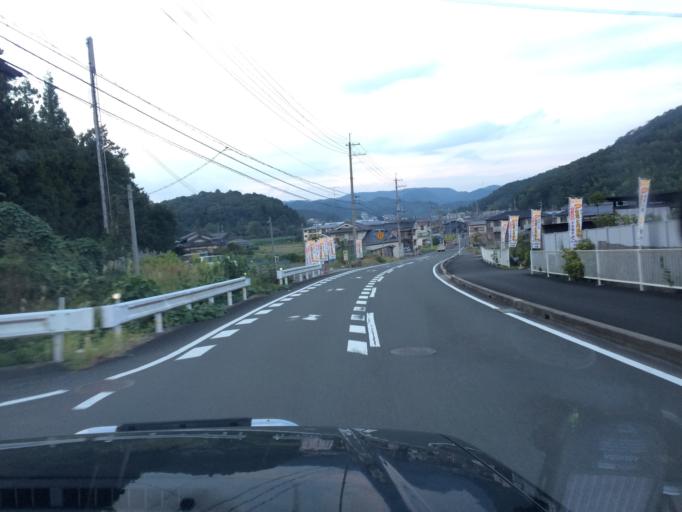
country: JP
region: Kyoto
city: Kameoka
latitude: 35.0933
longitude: 135.4751
